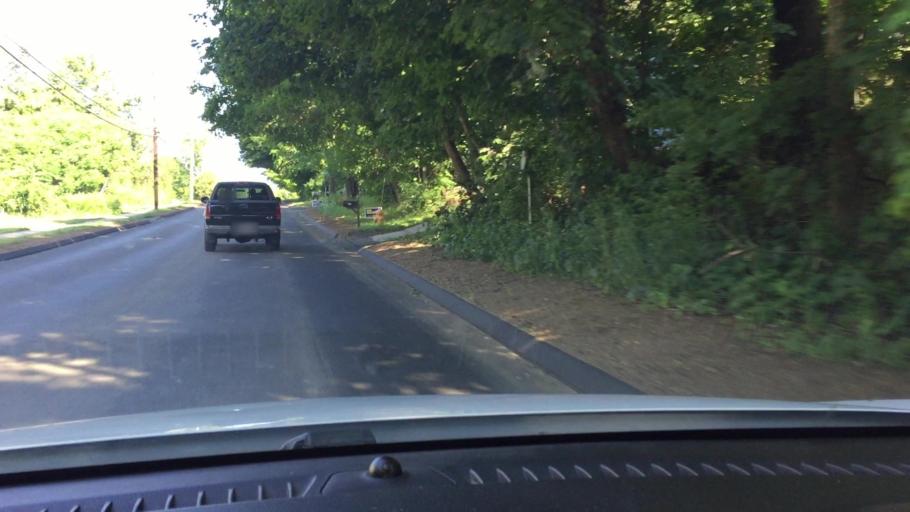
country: US
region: Massachusetts
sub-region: Berkshire County
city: Pittsfield
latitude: 42.4737
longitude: -73.2606
